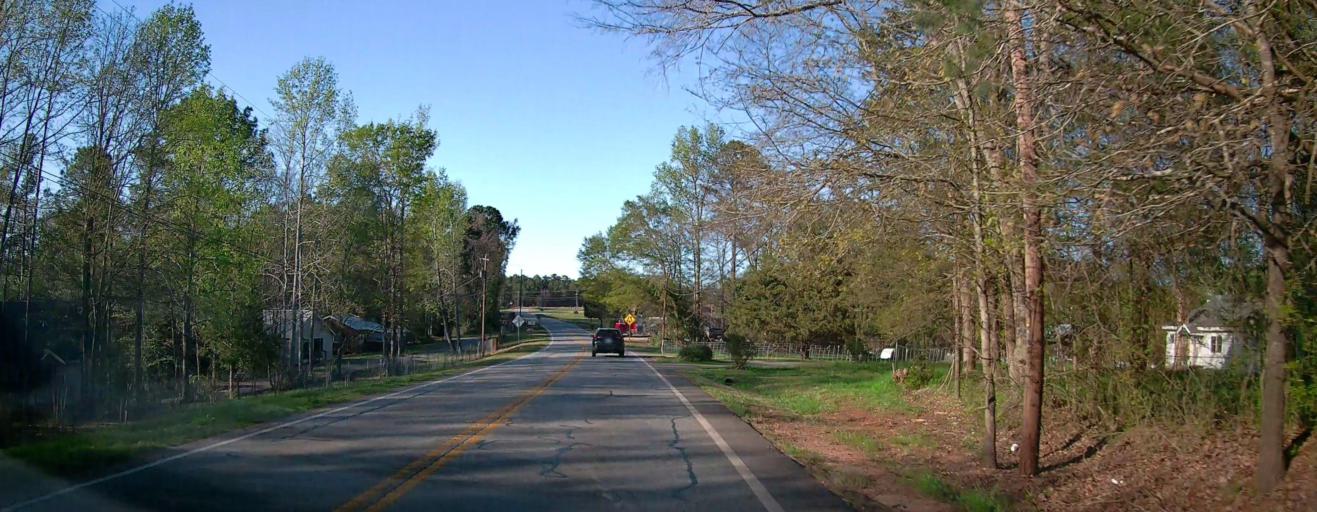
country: US
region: Georgia
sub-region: Butts County
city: Indian Springs
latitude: 33.2606
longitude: -83.9093
